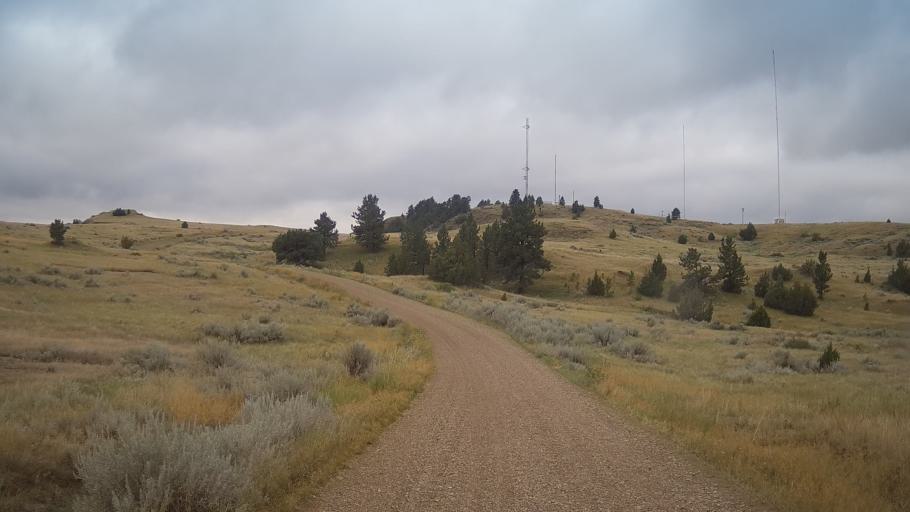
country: US
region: Montana
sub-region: Dawson County
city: Glendive
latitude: 47.0564
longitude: -104.6715
